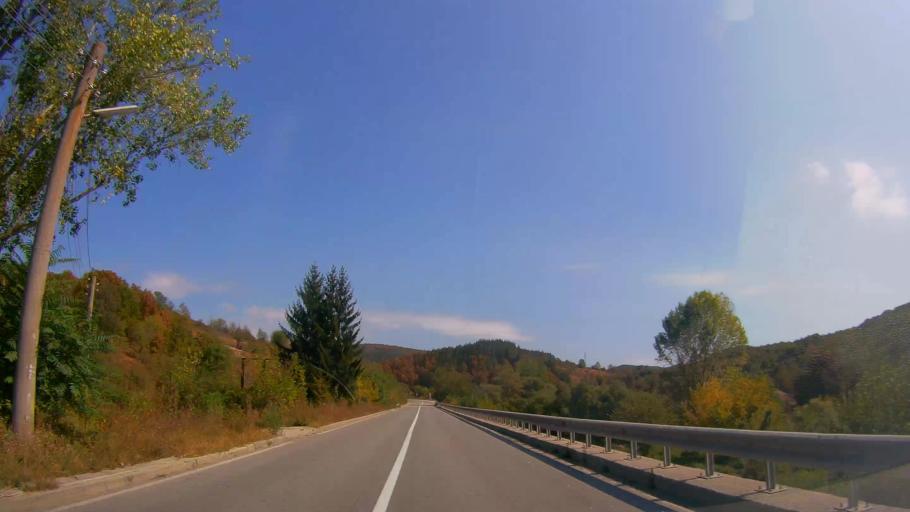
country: BG
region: Shumen
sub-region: Obshtina Smyadovo
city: Smyadovo
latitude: 42.9849
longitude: 27.0358
